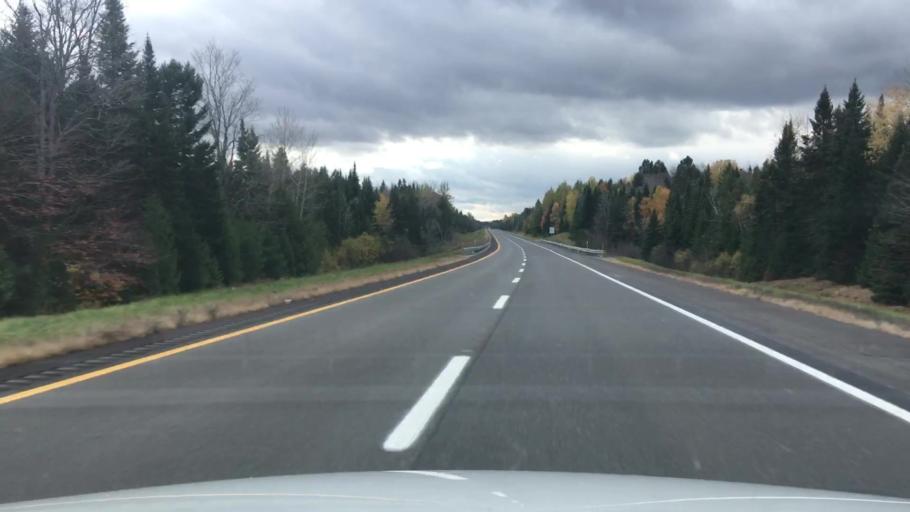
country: US
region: Maine
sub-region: Penobscot County
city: Patten
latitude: 46.0862
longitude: -68.2084
